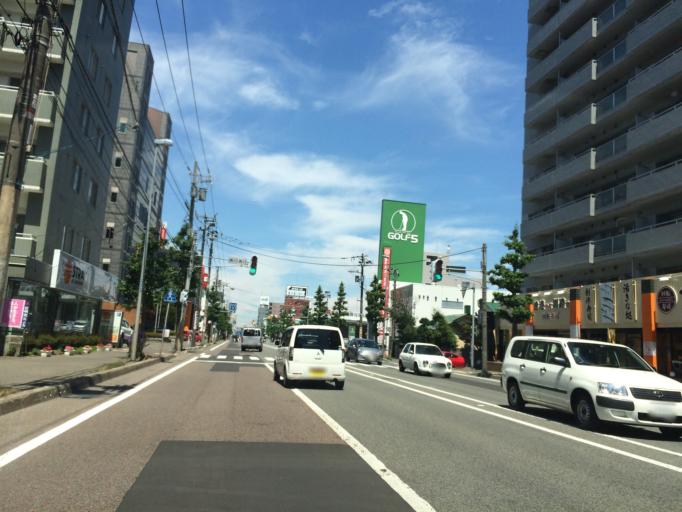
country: JP
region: Hokkaido
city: Sapporo
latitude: 43.0420
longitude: 141.3434
